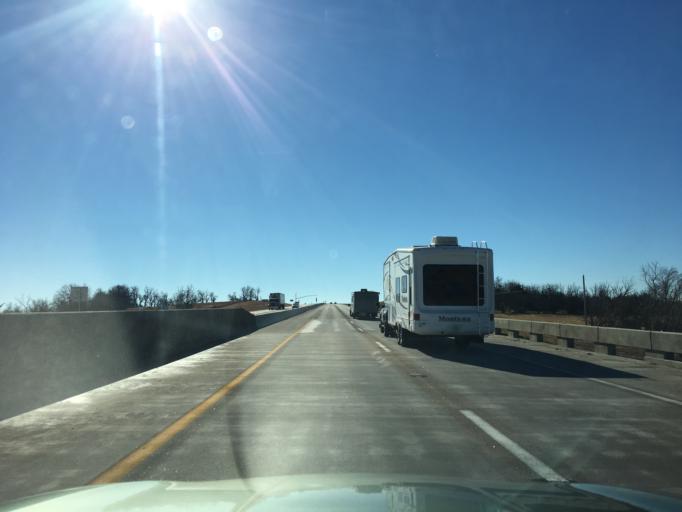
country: US
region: Oklahoma
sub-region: Kay County
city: Blackwell
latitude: 37.0066
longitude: -97.3404
